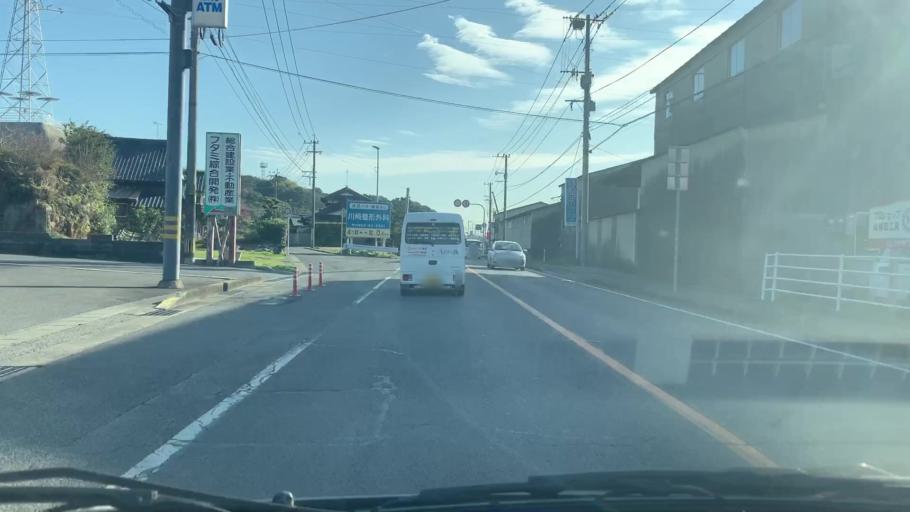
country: JP
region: Saga Prefecture
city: Takeocho-takeo
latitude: 33.2149
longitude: 130.0942
